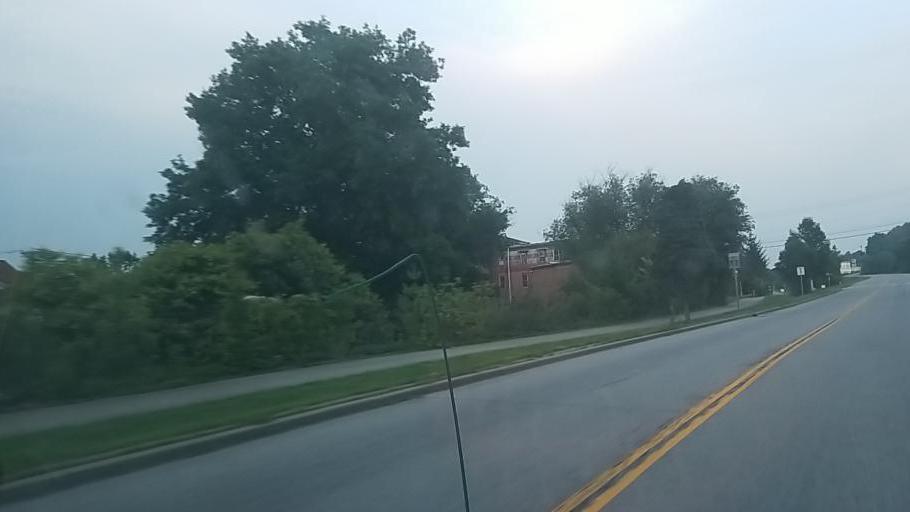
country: US
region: New York
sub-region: Montgomery County
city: Fonda
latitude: 42.9468
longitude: -74.3730
